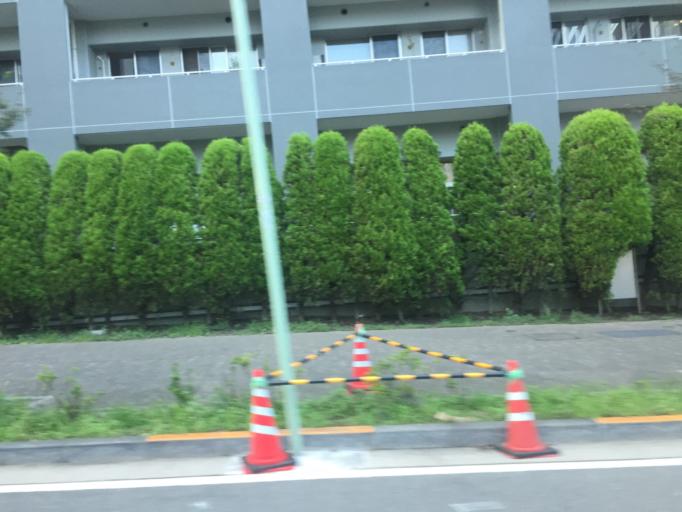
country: JP
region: Kanagawa
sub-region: Kawasaki-shi
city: Kawasaki
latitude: 35.5643
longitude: 139.6833
